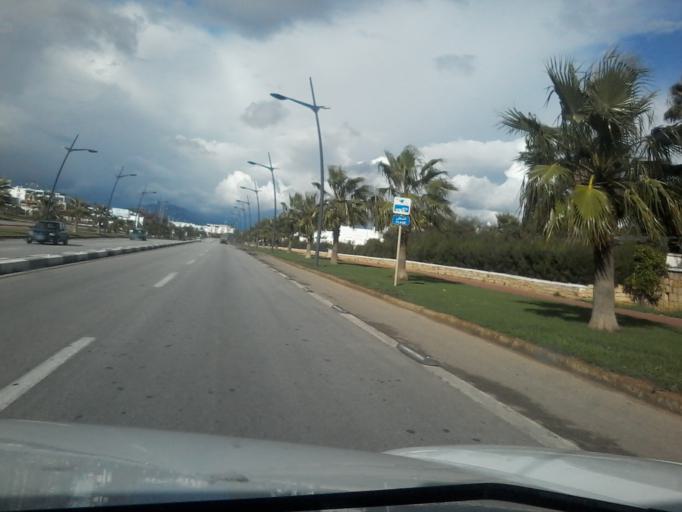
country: MA
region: Tanger-Tetouan
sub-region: Tetouan
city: Martil
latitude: 35.7378
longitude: -5.3424
